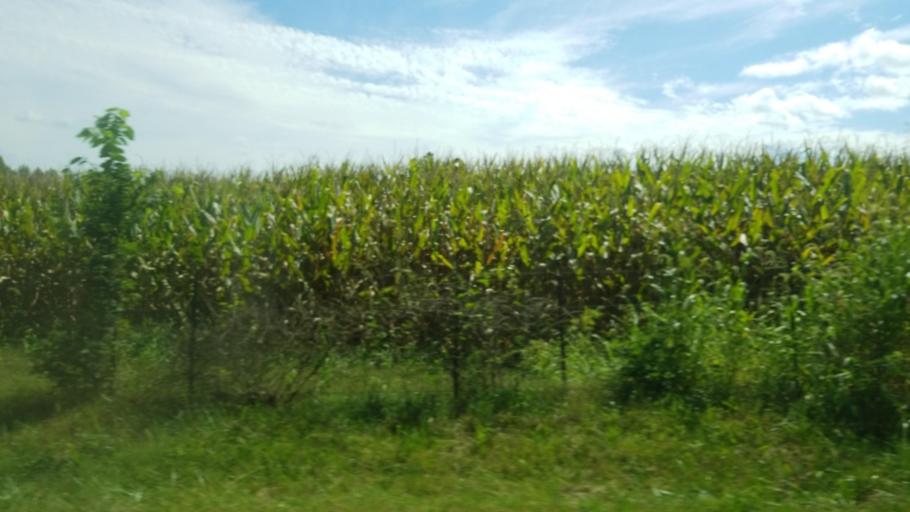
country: US
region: Illinois
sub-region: Williamson County
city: Johnston City
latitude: 37.7902
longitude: -88.8205
